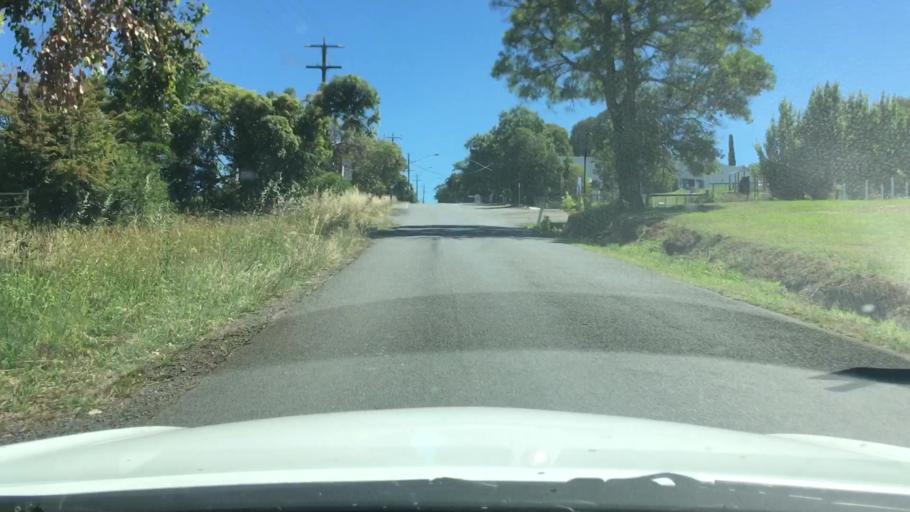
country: AU
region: Victoria
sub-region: Yarra Ranges
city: Mount Evelyn
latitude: -37.7897
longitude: 145.4380
